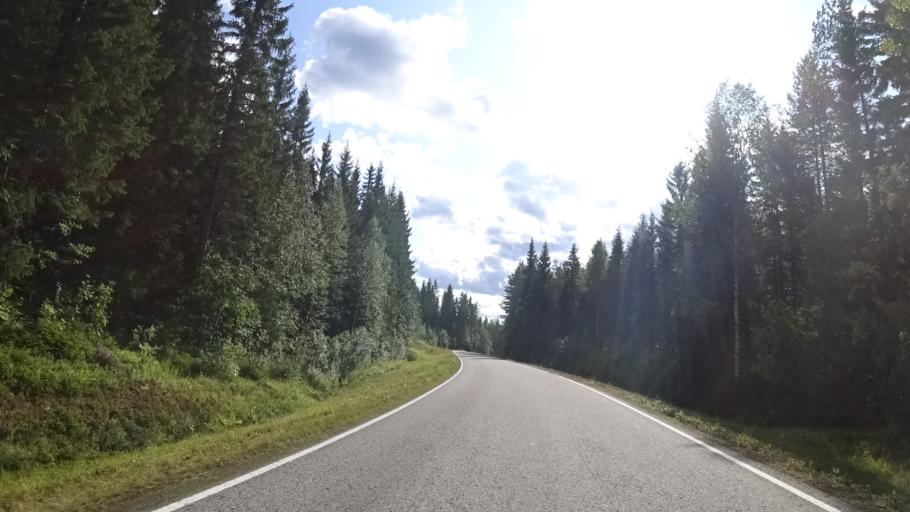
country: RU
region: Republic of Karelia
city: Vyartsilya
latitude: 62.2428
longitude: 30.7075
